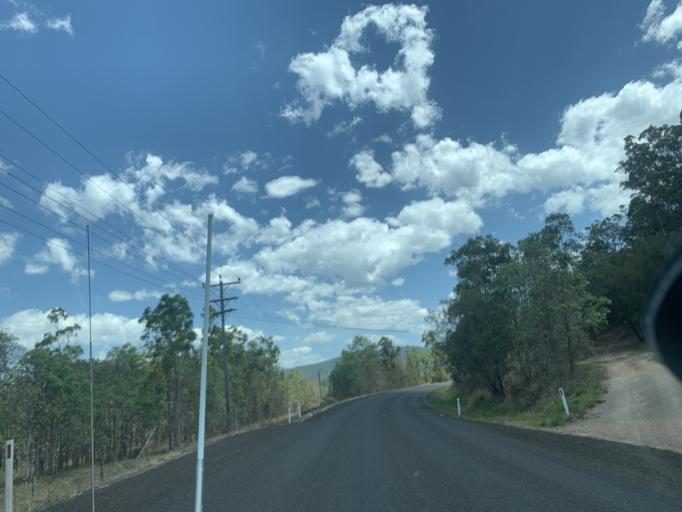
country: AU
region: Queensland
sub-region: Tablelands
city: Atherton
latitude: -17.2980
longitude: 145.4726
